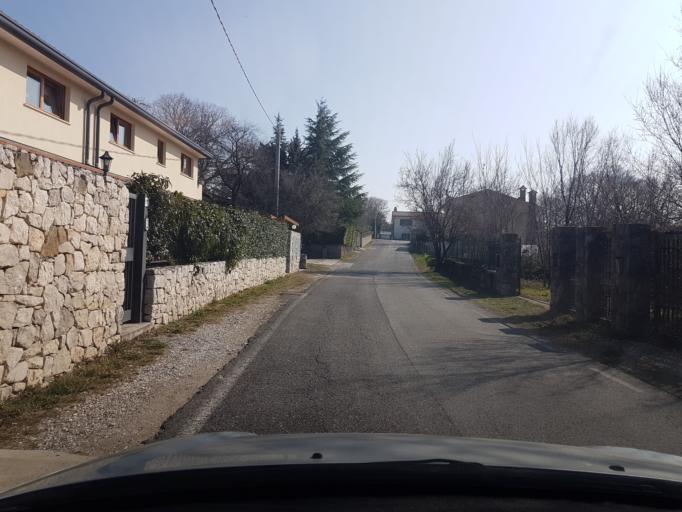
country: IT
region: Friuli Venezia Giulia
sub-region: Provincia di Trieste
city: Sistiana-Visogliano
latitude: 45.7741
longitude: 13.6418
